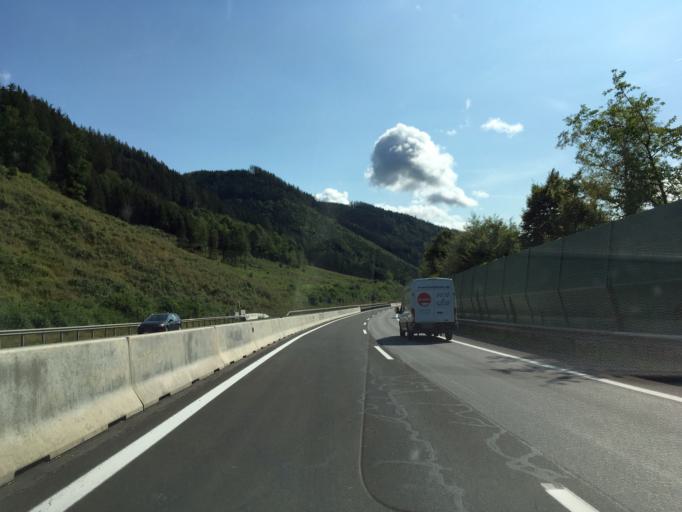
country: AT
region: Styria
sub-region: Politischer Bezirk Leoben
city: Leoben
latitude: 47.3606
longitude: 15.1072
